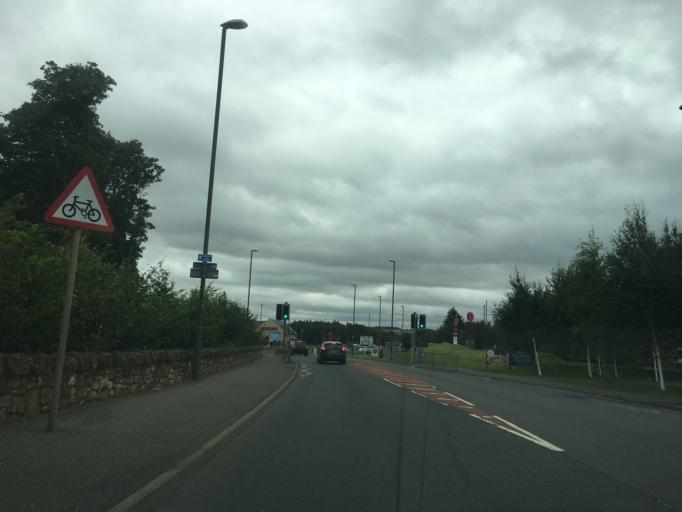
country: GB
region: Scotland
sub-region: Midlothian
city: Bonnyrigg
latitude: 55.8967
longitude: -3.1004
